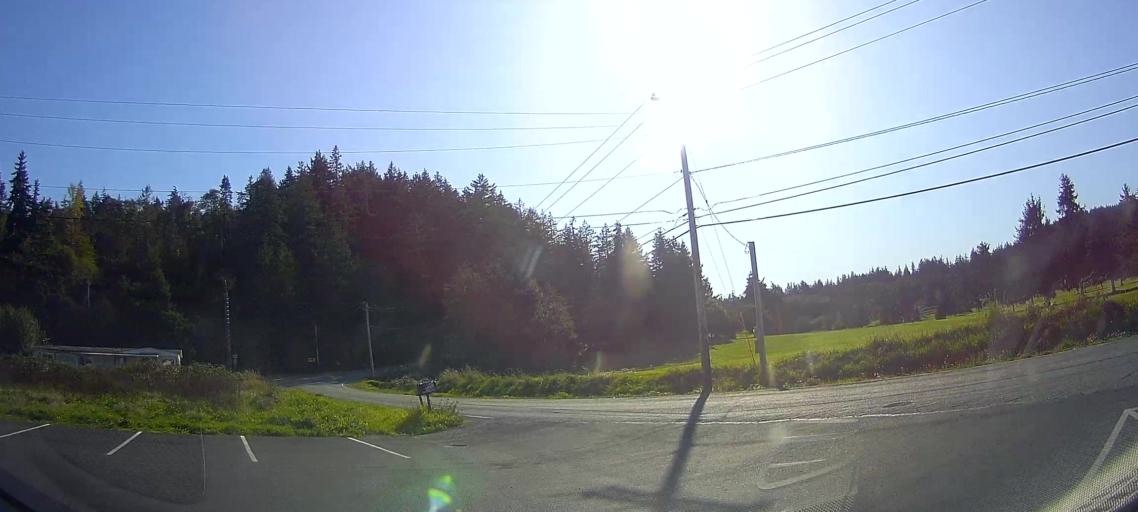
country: US
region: Washington
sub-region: Skagit County
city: Anacortes
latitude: 48.4613
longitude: -122.5708
